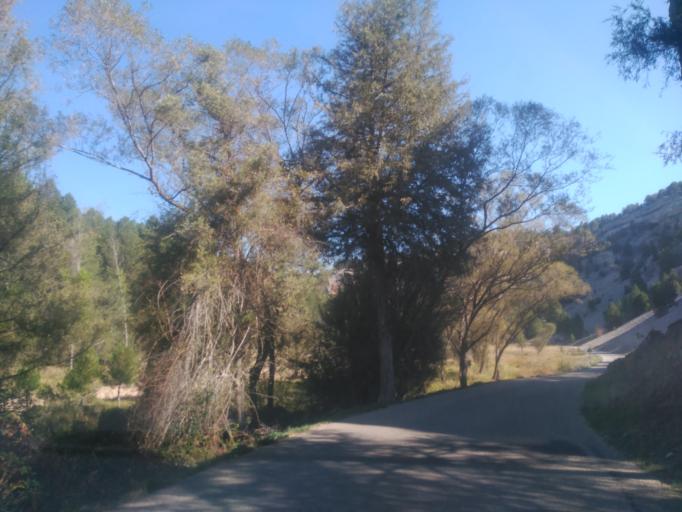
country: ES
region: Castille and Leon
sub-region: Provincia de Soria
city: Ucero
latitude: 41.7416
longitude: -3.0598
